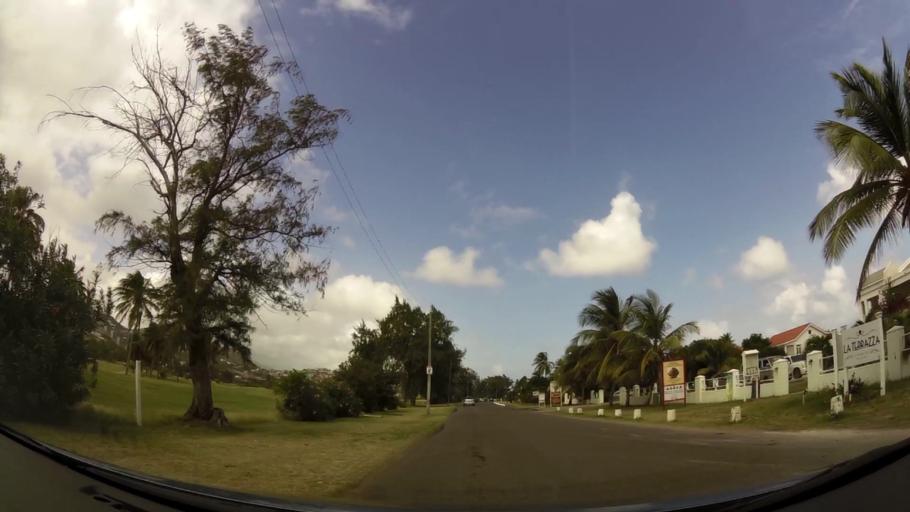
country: KN
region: Saint George Basseterre
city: Basseterre
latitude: 17.2847
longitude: -62.6850
